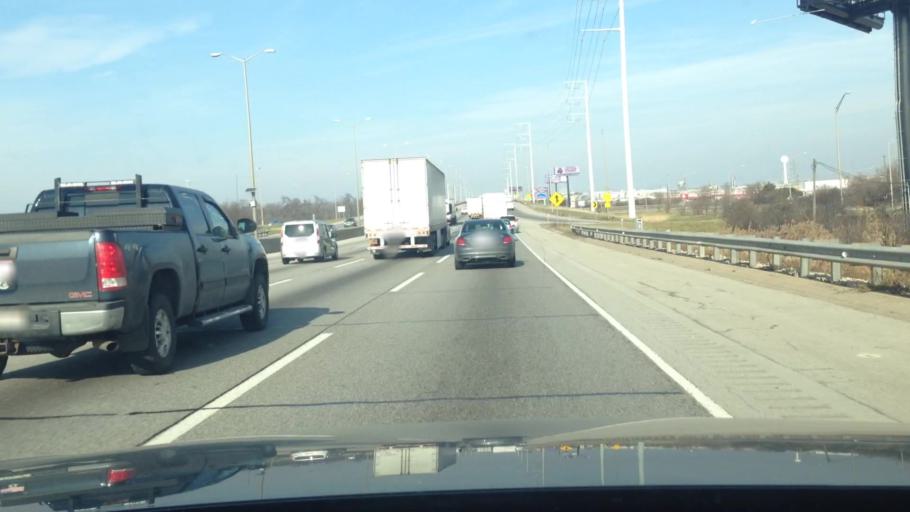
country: US
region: Illinois
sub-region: Cook County
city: Berkeley
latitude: 41.9014
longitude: -87.9187
